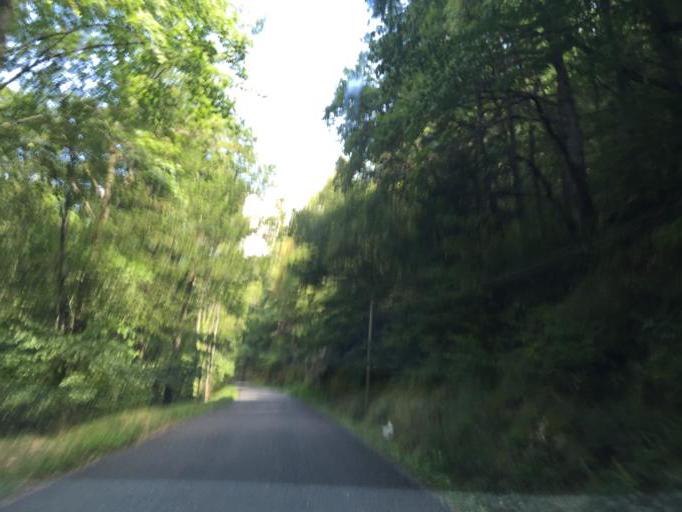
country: FR
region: Rhone-Alpes
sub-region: Departement de la Loire
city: Saint-Jean-Bonnefonds
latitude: 45.4170
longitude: 4.4469
